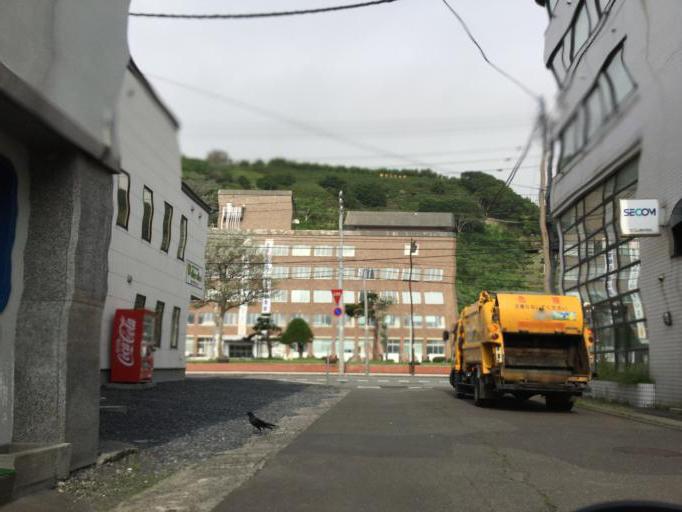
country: JP
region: Hokkaido
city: Wakkanai
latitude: 45.4158
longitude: 141.6746
